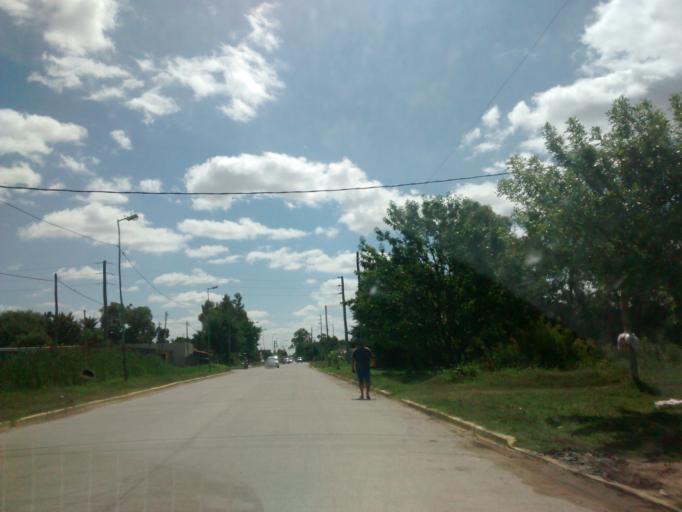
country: AR
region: Buenos Aires
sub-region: Partido de Berisso
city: Berisso
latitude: -34.8898
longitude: -57.8709
